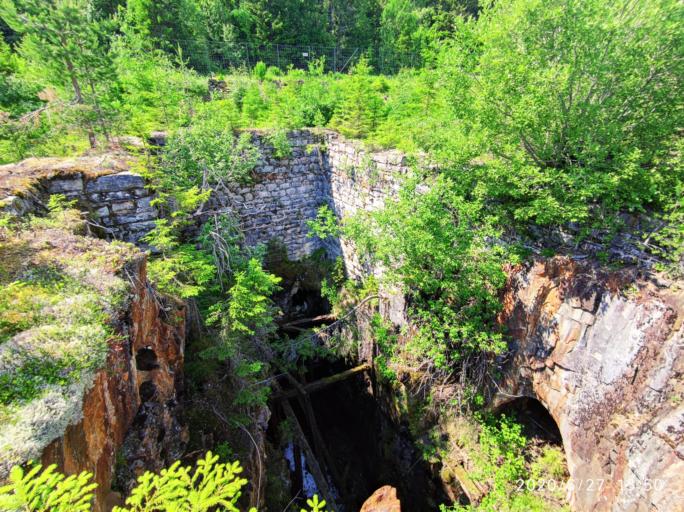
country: NO
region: Buskerud
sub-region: Kongsberg
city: Kongsberg
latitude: 59.6604
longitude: 9.5868
